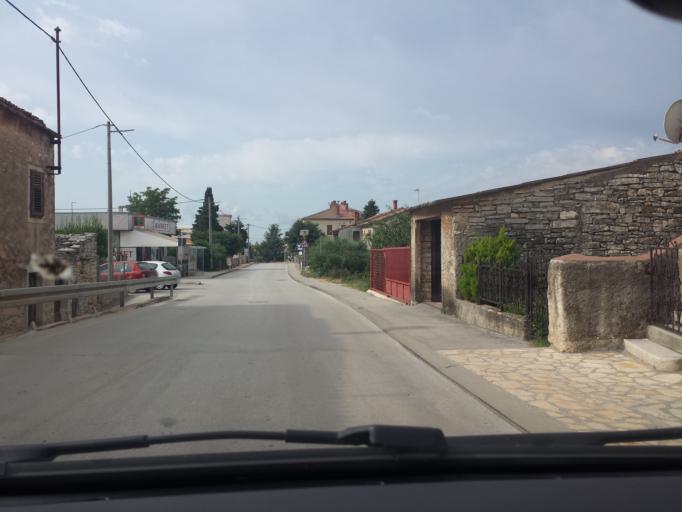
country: HR
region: Istarska
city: Galizana
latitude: 44.9323
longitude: 13.8690
